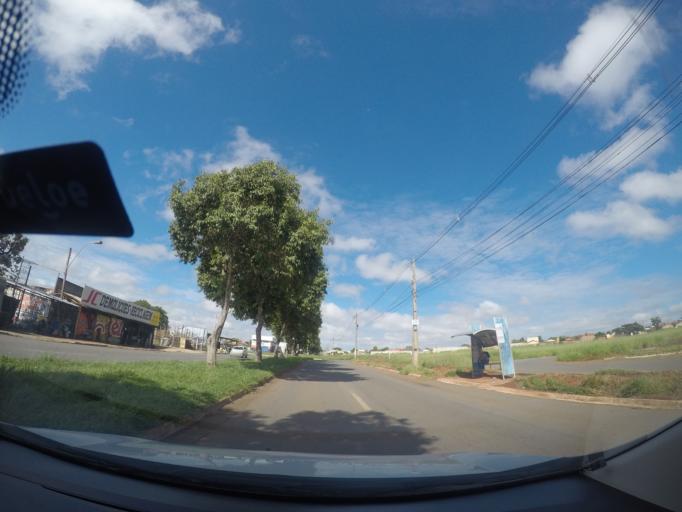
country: BR
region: Goias
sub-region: Goiania
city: Goiania
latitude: -16.6535
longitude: -49.1753
